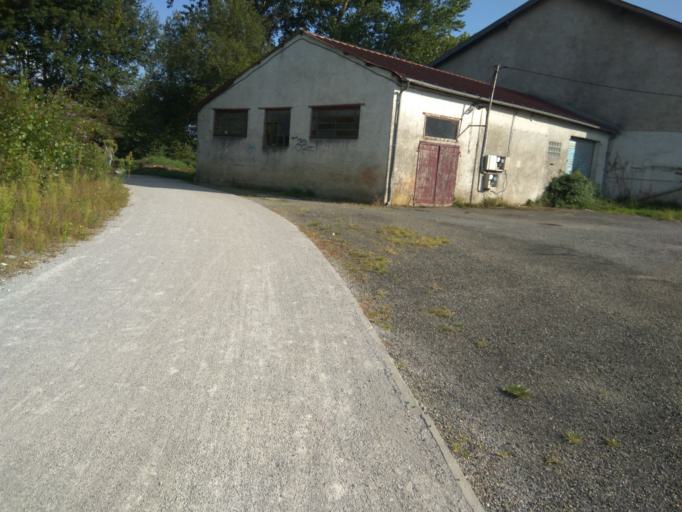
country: FR
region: Aquitaine
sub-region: Departement des Pyrenees-Atlantiques
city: Jurancon
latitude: 43.2910
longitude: -0.3766
